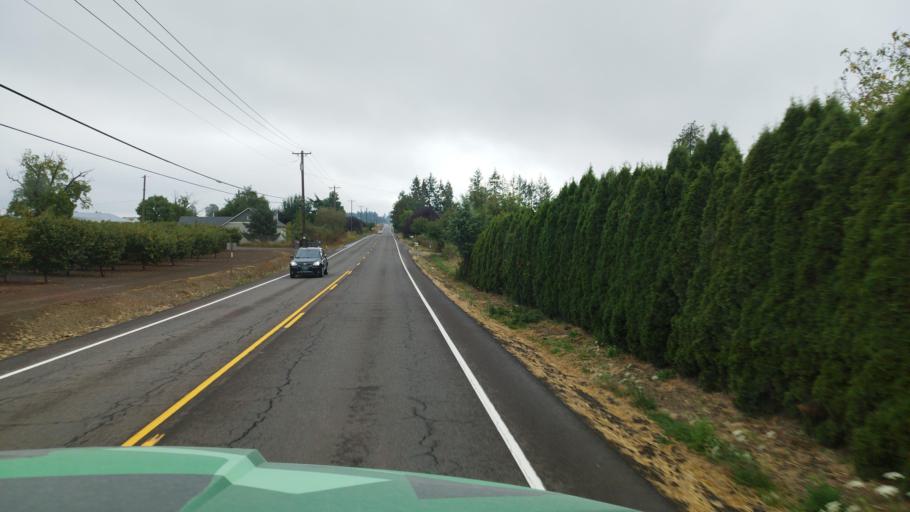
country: US
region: Oregon
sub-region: Yamhill County
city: Yamhill
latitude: 45.3303
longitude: -123.1835
